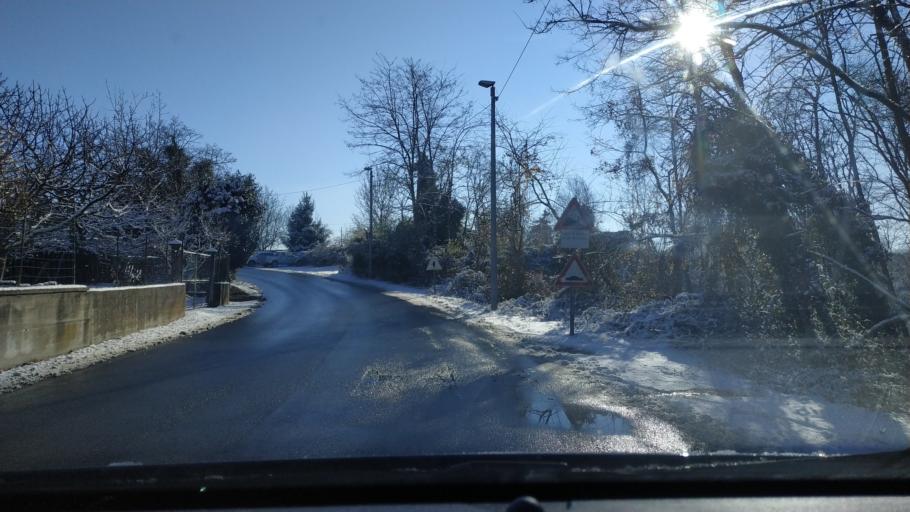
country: IT
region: Piedmont
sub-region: Provincia di Torino
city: Candia Canavese
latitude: 45.3264
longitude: 7.8866
